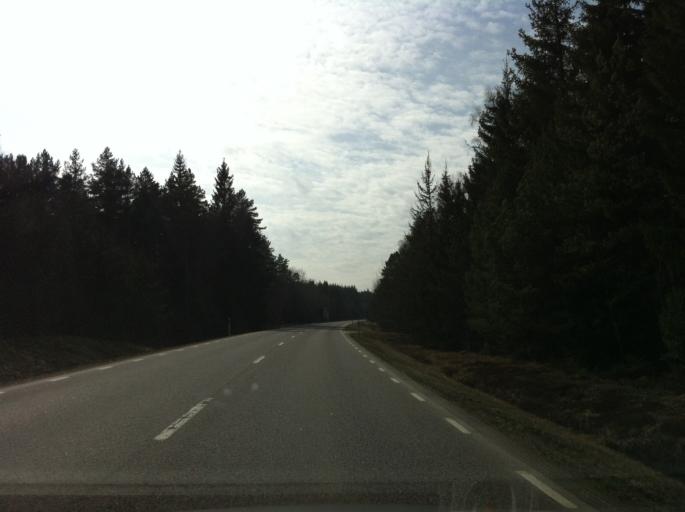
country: SE
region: Vaestra Goetaland
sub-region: Falkopings Kommun
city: Floby
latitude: 58.1424
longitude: 13.3578
